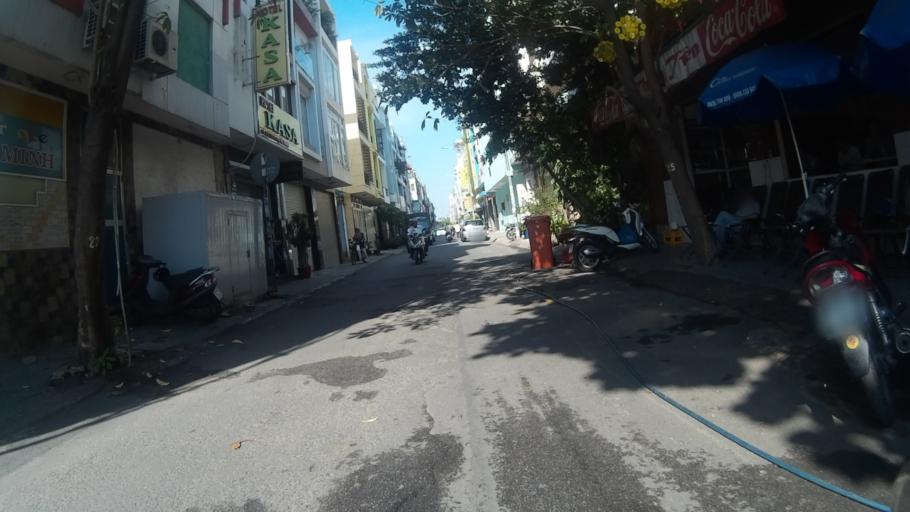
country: VN
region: Ho Chi Minh City
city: Quan Binh Thanh
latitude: 10.7969
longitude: 106.6903
